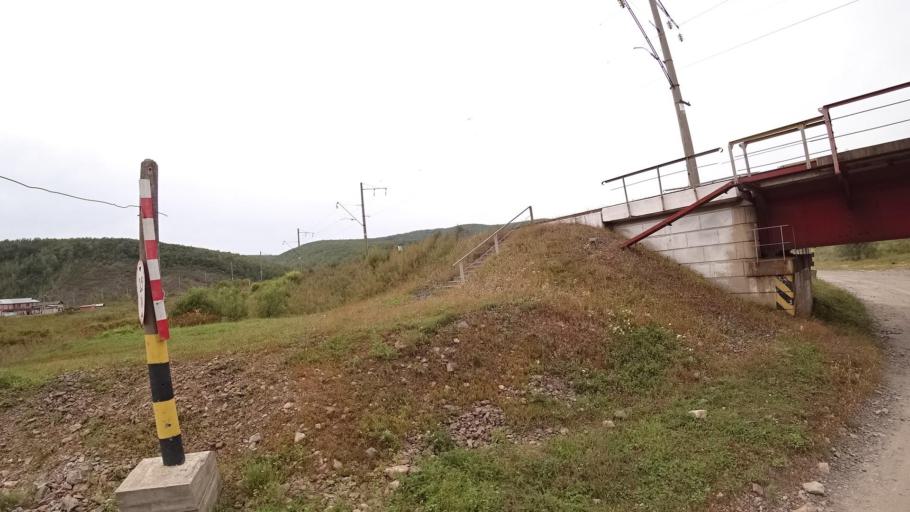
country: RU
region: Jewish Autonomous Oblast
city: Khingansk
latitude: 49.0301
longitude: 131.0507
